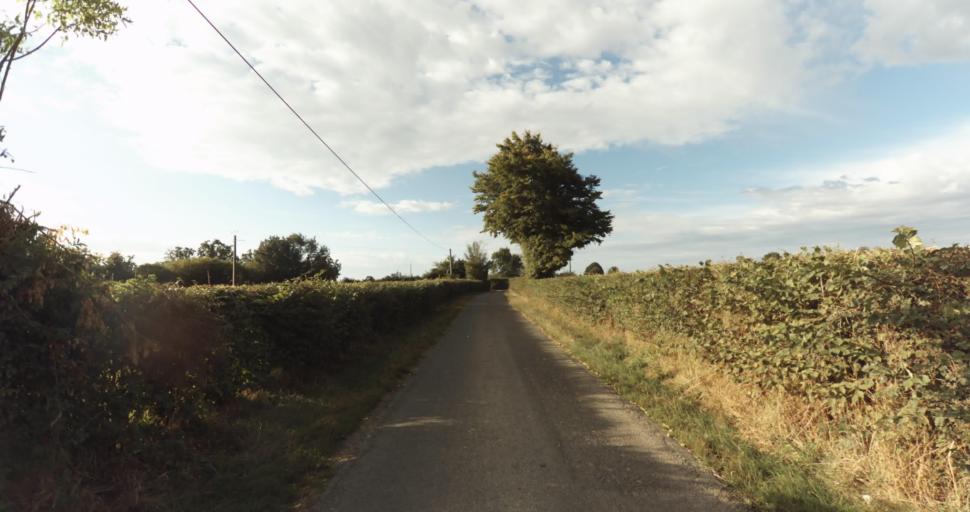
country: FR
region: Lower Normandy
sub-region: Departement de l'Orne
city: Vimoutiers
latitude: 48.9429
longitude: 0.2519
